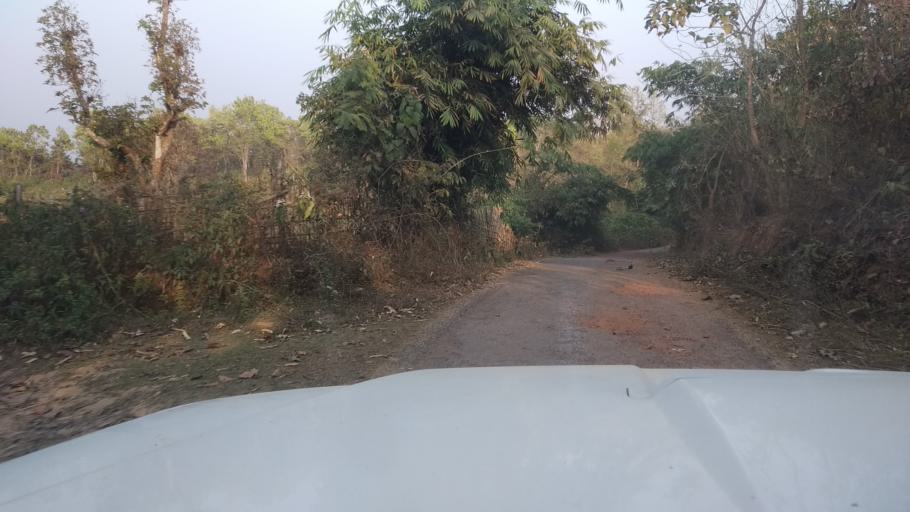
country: IN
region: Tripura
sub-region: South Tripura
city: Belonia
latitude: 23.3184
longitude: 91.3158
